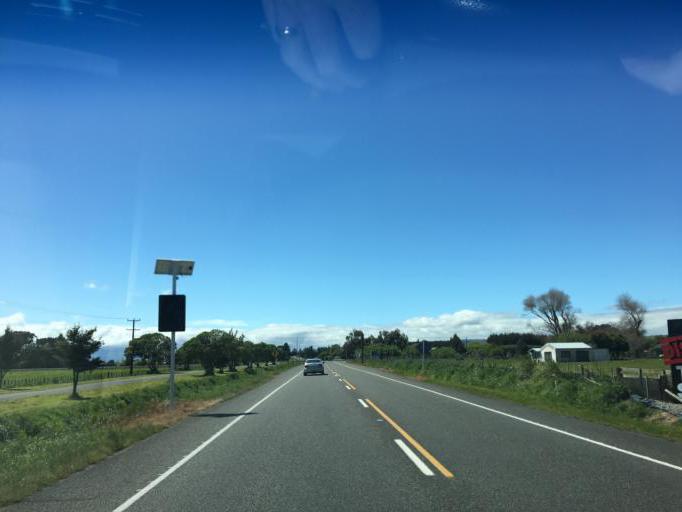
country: NZ
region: Manawatu-Wanganui
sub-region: Palmerston North City
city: Palmerston North
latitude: -40.3812
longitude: 175.5505
